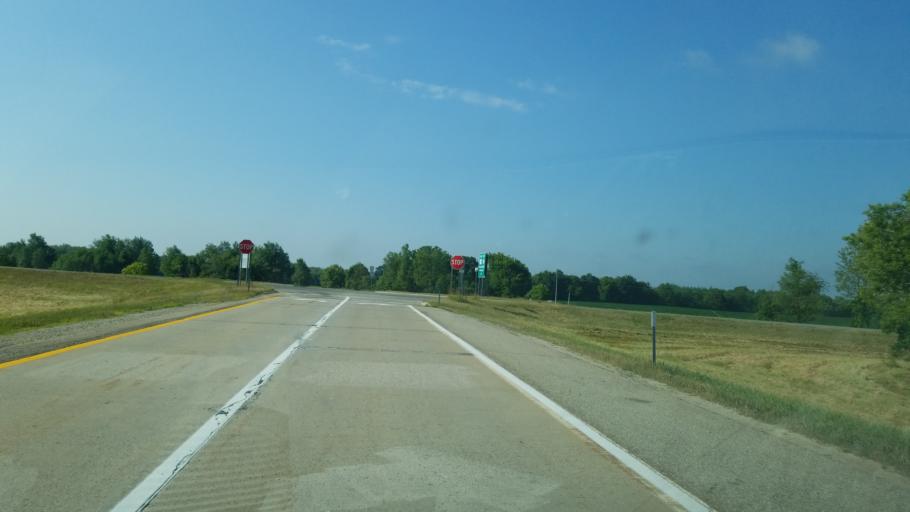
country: US
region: Michigan
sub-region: Kent County
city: Cedar Springs
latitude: 43.2948
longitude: -85.5458
